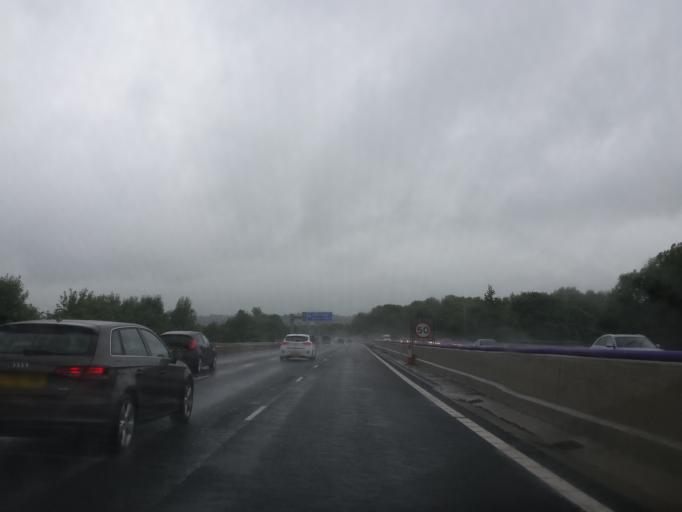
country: GB
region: England
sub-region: Derbyshire
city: Blackwell
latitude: 53.1243
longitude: -1.3312
